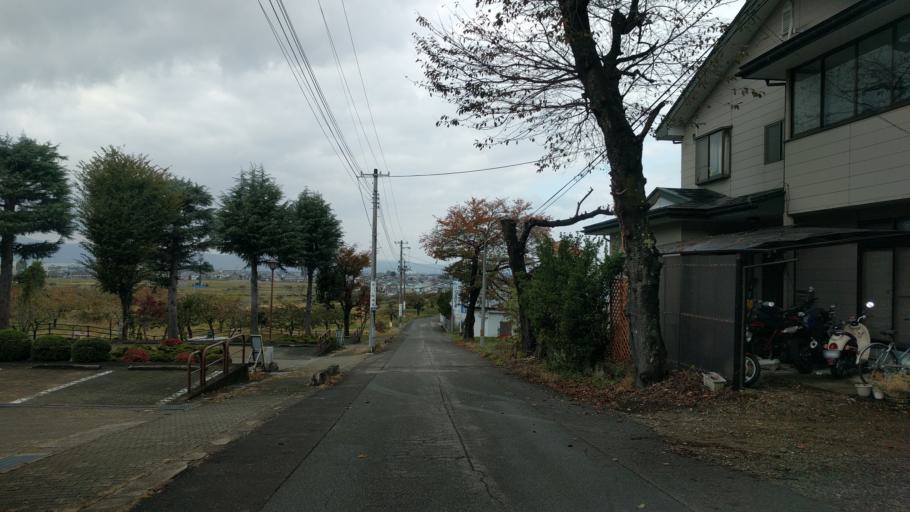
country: JP
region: Fukushima
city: Kitakata
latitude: 37.4694
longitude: 139.9381
